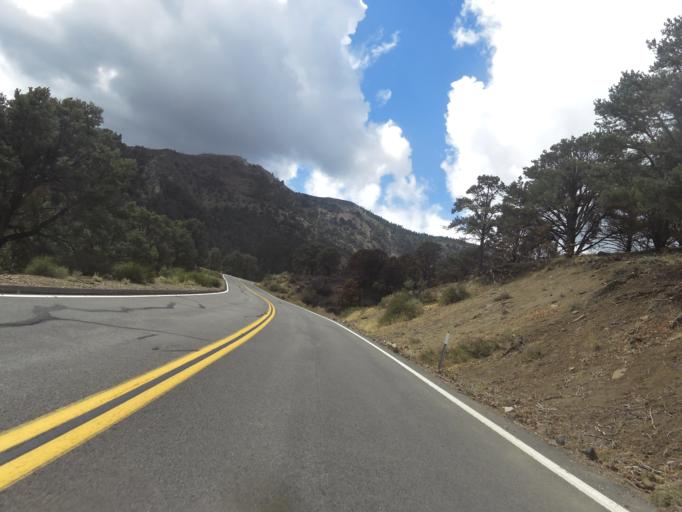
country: US
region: Nevada
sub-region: Lyon County
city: Smith Valley
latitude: 38.6557
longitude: -119.5894
